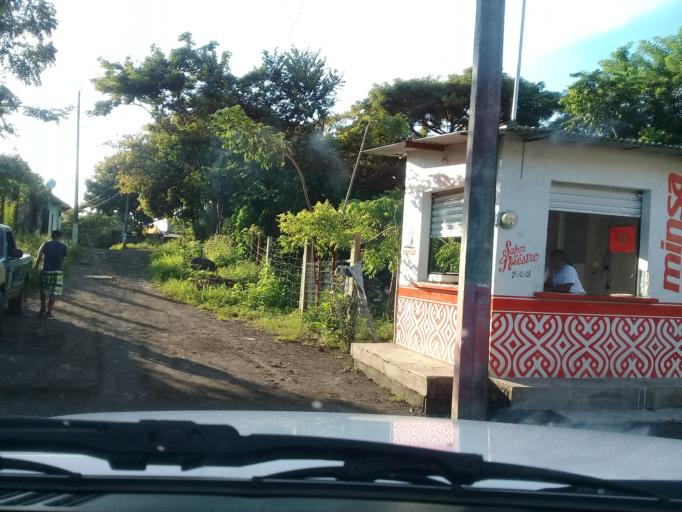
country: MX
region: Veracruz
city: Catemaco
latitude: 18.4232
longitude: -95.1008
